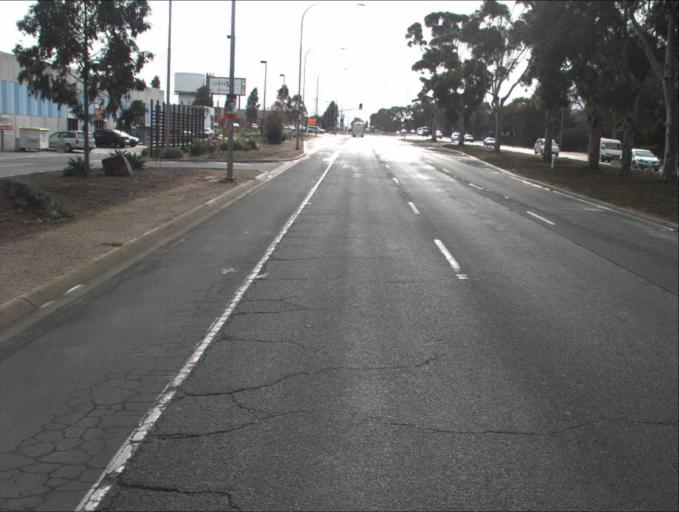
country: AU
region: South Australia
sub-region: Port Adelaide Enfield
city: Enfield
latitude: -34.8391
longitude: 138.6067
